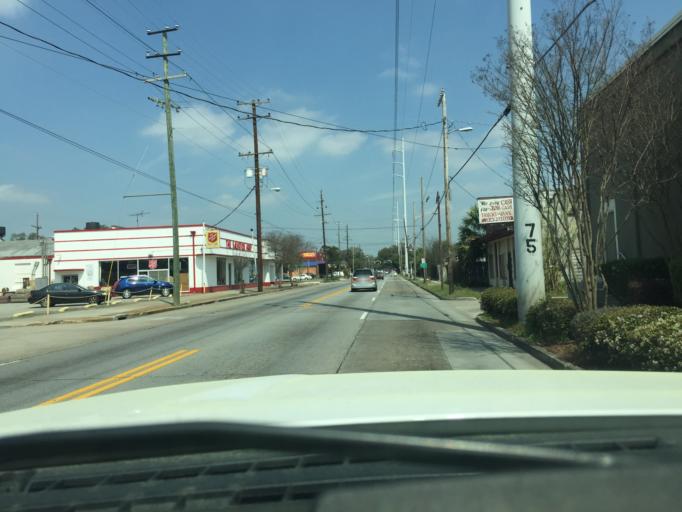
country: US
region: Georgia
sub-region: Chatham County
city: Savannah
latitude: 32.0505
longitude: -81.1072
